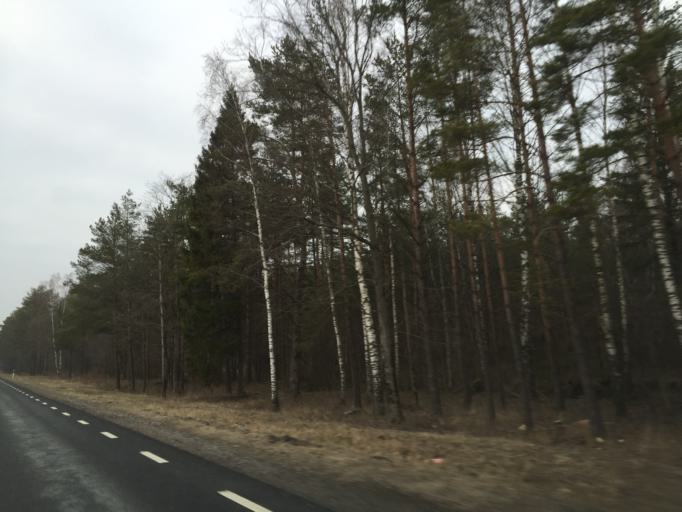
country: EE
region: Saare
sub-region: Orissaare vald
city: Orissaare
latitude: 58.5941
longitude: 23.3292
